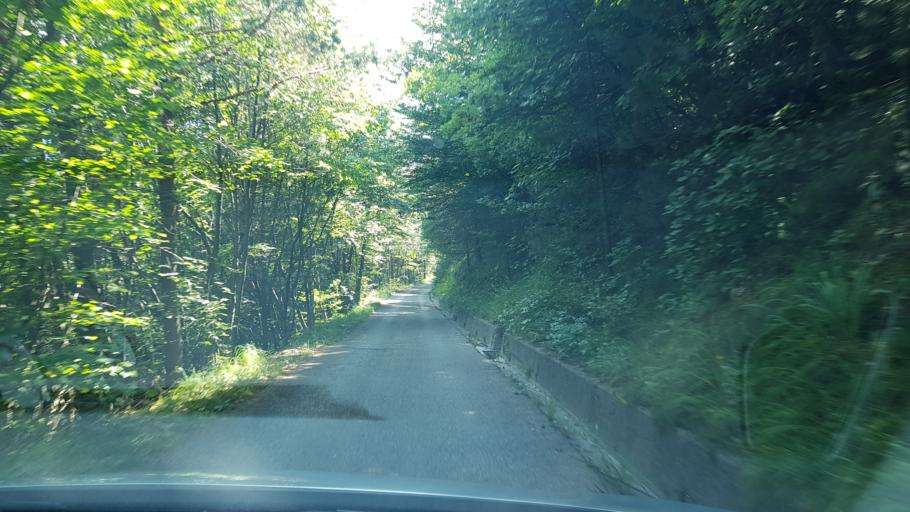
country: IT
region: Friuli Venezia Giulia
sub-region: Provincia di Udine
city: Moggio Udinese
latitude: 46.4365
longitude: 13.2123
